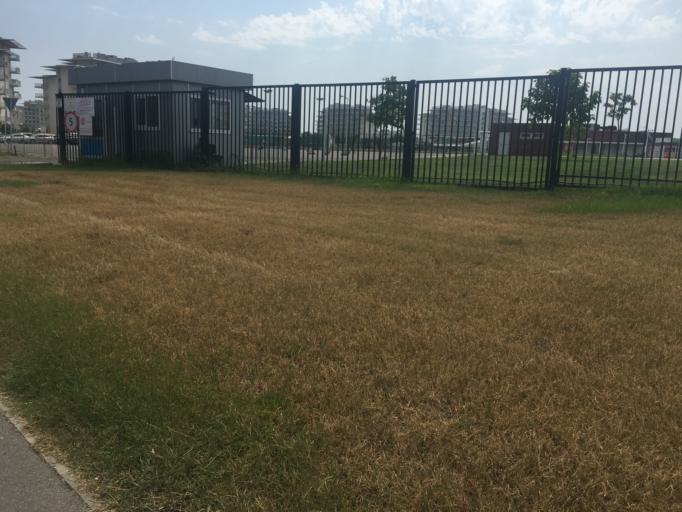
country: RU
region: Krasnodarskiy
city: Adler
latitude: 43.4062
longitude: 39.9741
